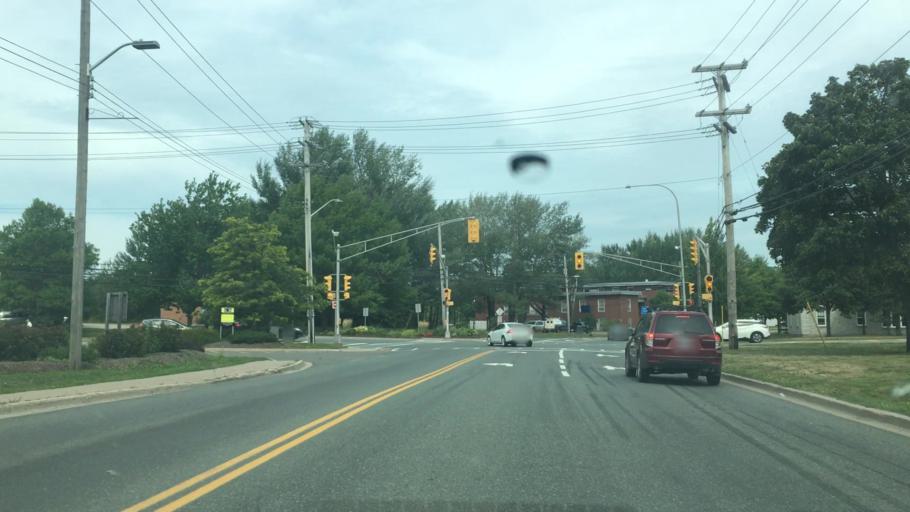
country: CA
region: Nova Scotia
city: Antigonish
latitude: 45.6160
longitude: -61.9990
